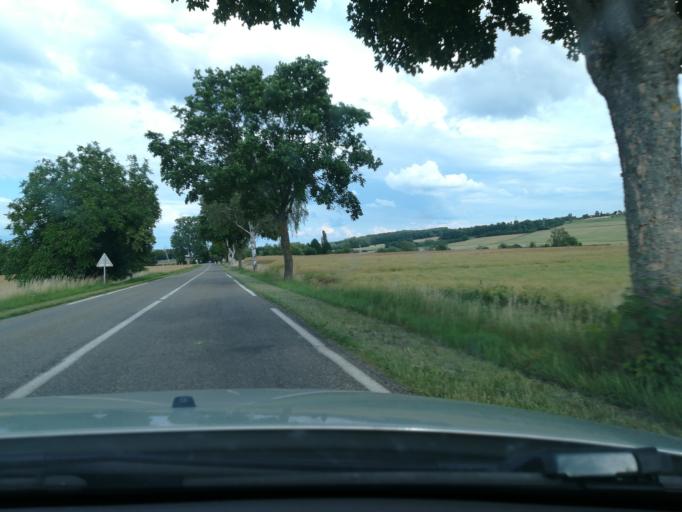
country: FR
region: Alsace
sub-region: Departement du Bas-Rhin
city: Obermodern-Zutzendorf
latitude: 48.8409
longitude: 7.5414
